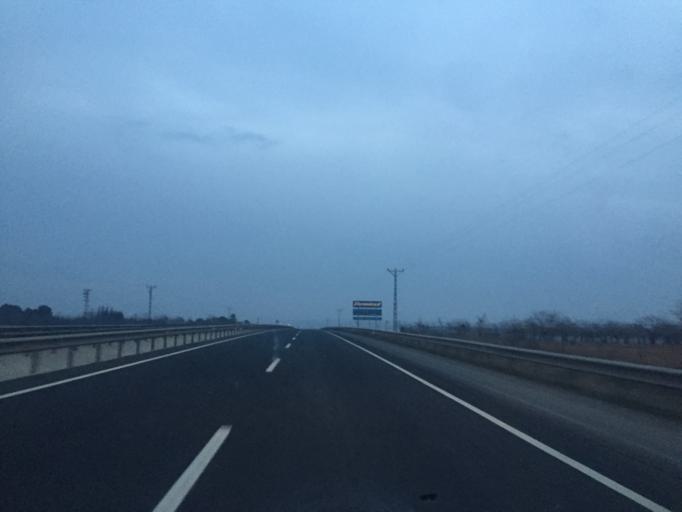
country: TR
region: Sanliurfa
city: Camlidere
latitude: 37.1528
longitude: 39.0720
